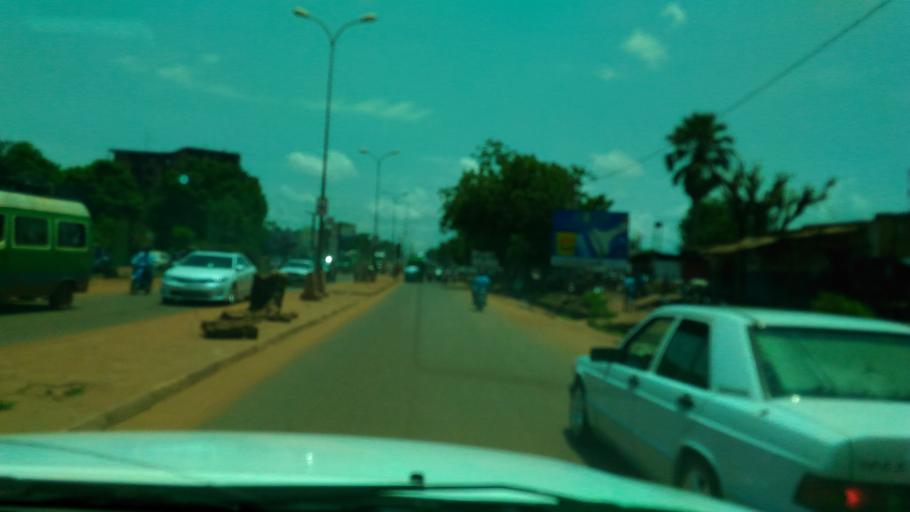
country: ML
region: Bamako
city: Bamako
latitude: 12.6573
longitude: -7.9682
